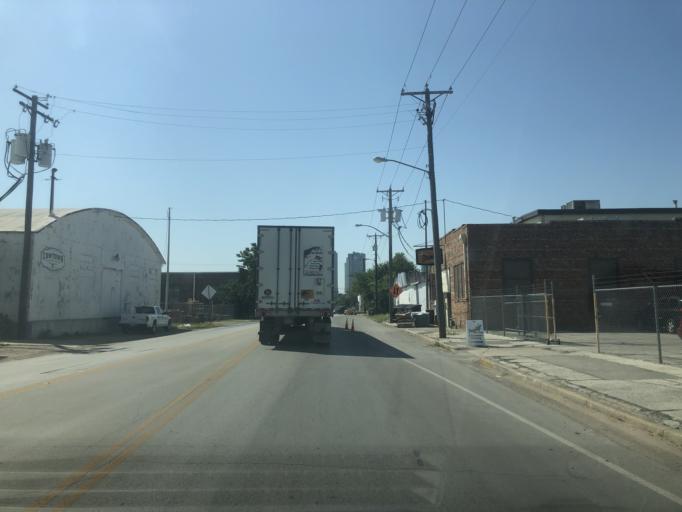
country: US
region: Texas
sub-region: Tarrant County
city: Fort Worth
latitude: 32.7699
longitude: -97.3405
